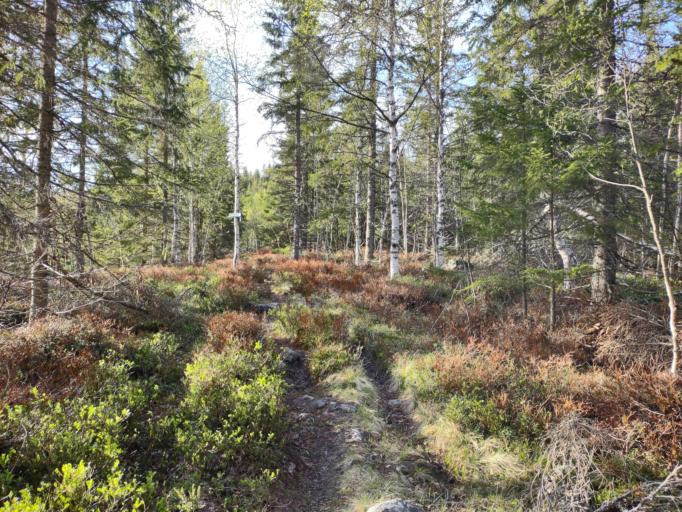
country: NO
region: Akershus
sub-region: Nittedal
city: Aneby
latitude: 60.2376
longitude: 10.8544
